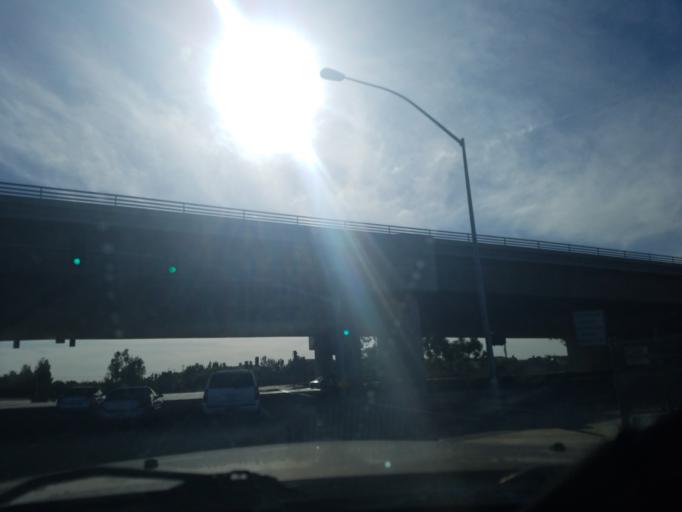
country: US
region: California
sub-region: Orange County
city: Irvine
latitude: 33.7046
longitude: -117.8065
